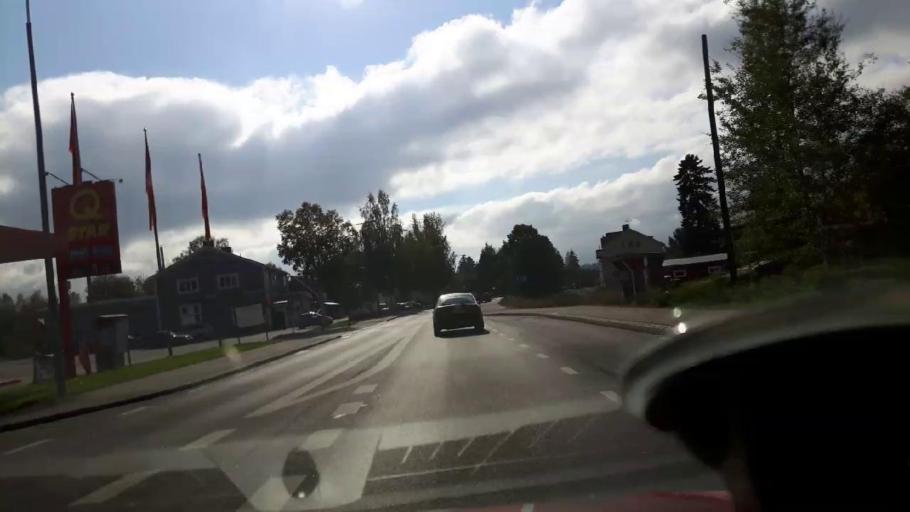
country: SE
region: Gaevleborg
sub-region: Bollnas Kommun
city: Arbra
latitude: 61.5182
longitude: 16.3632
